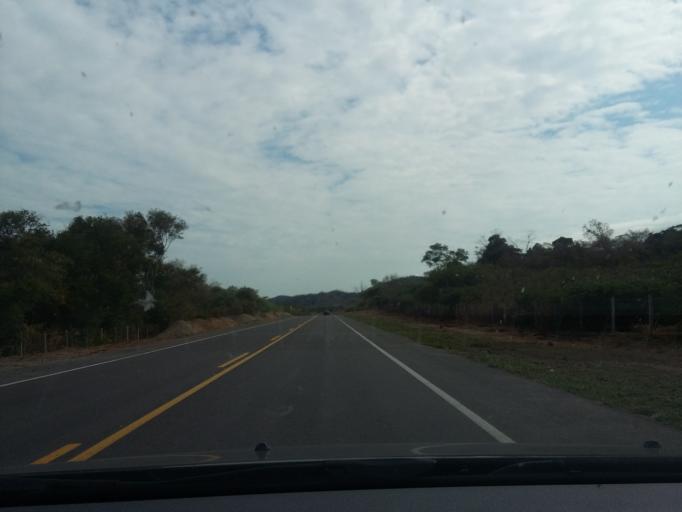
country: CO
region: Tolima
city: Ambalema
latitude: 4.6972
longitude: -74.7864
